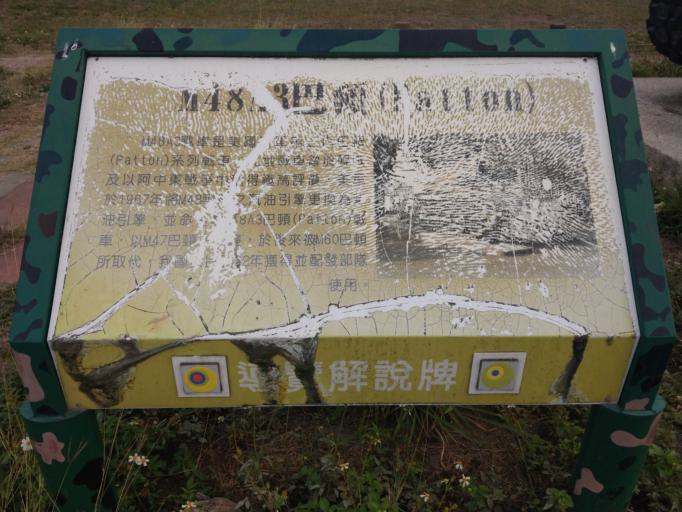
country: TW
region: Taiwan
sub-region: Pingtung
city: Pingtung
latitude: 22.7844
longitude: 120.4949
